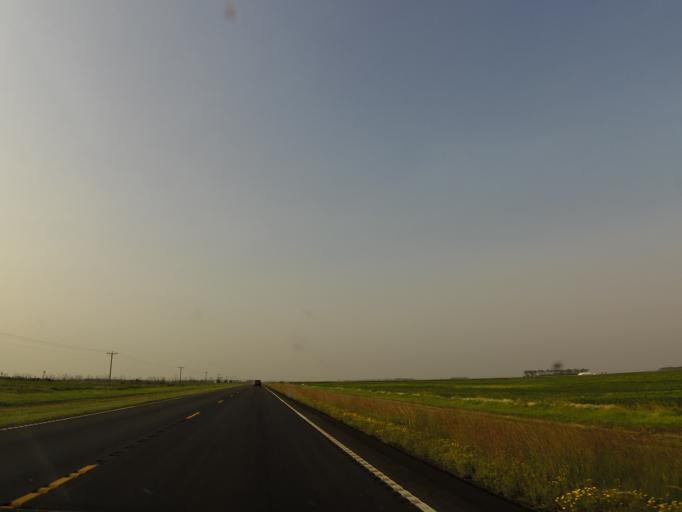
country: US
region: North Dakota
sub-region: Traill County
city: Mayville
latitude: 47.4049
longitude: -97.3265
